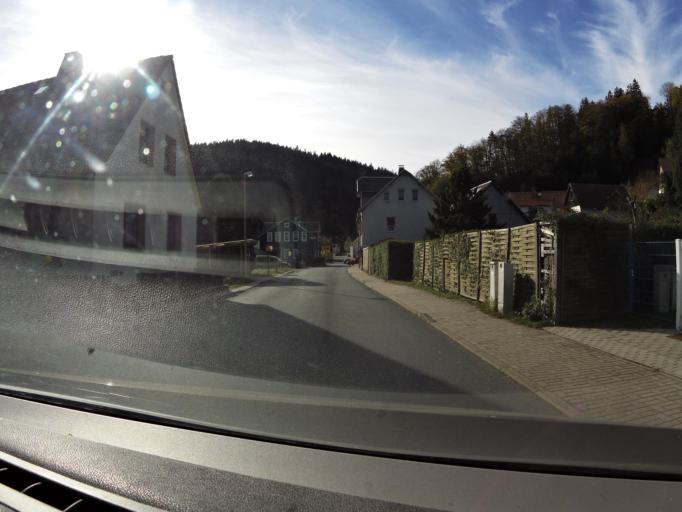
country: DE
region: Thuringia
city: Geraberg
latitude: 50.7145
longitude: 10.8267
